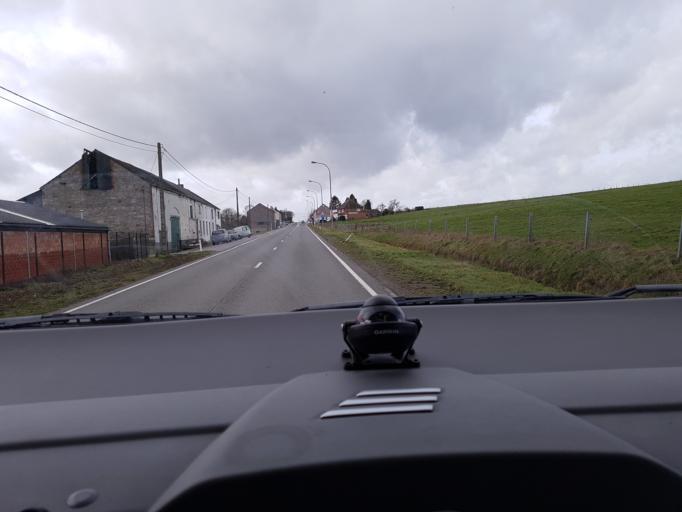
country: BE
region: Wallonia
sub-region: Province de Namur
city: Walcourt
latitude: 50.2255
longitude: 4.3927
